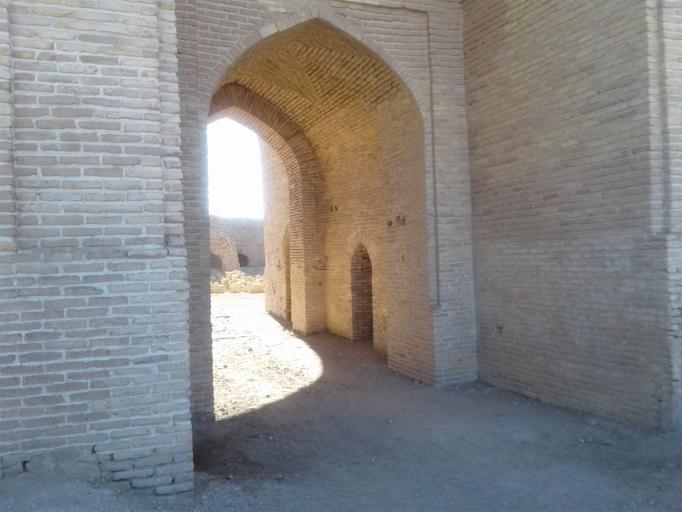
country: TM
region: Mary
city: Seydi
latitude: 40.0750
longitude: 62.3990
